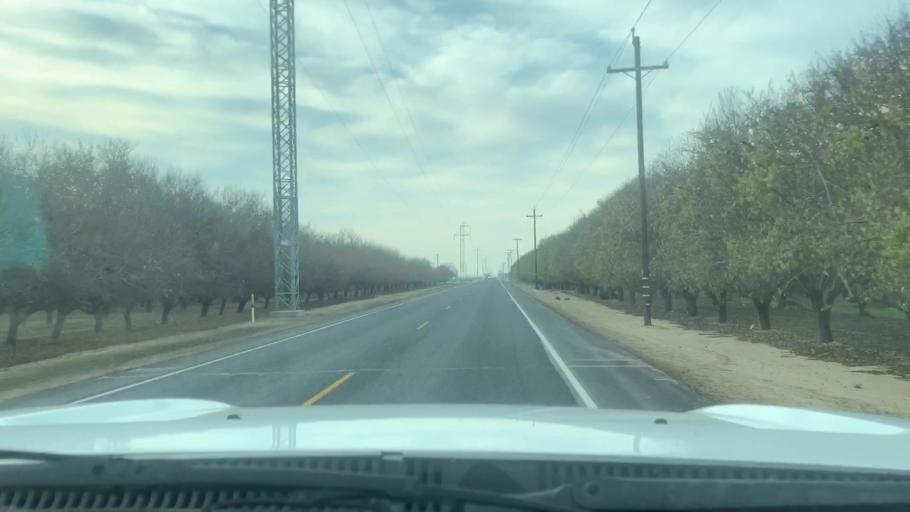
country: US
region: California
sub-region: Kern County
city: Shafter
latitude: 35.4419
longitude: -119.3021
